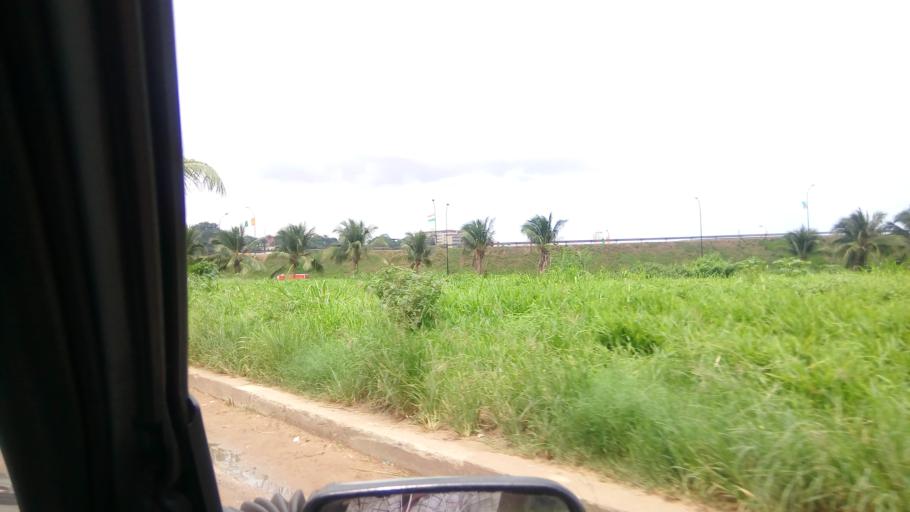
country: CI
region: Lagunes
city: Abidjan
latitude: 5.3409
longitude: -4.0177
